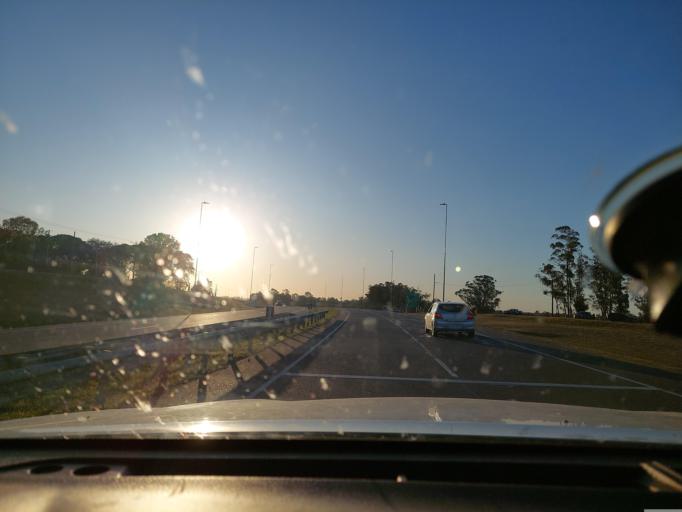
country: UY
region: Canelones
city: Empalme Olmos
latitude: -34.7000
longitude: -55.9160
